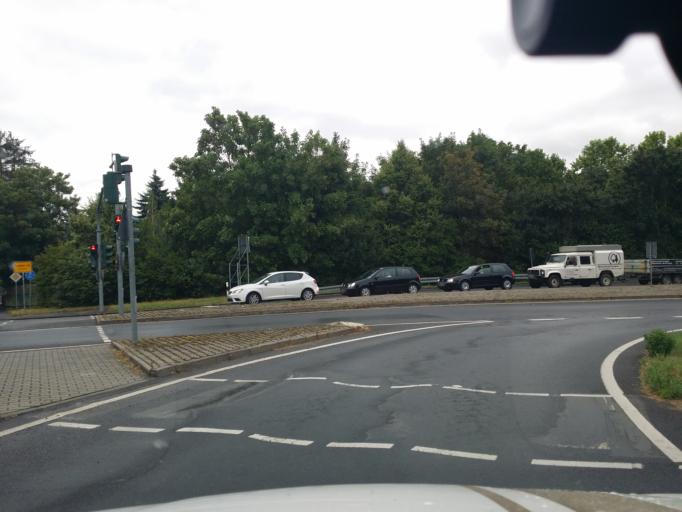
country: DE
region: Hesse
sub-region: Regierungsbezirk Darmstadt
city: Kriftel
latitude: 50.0962
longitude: 8.4851
